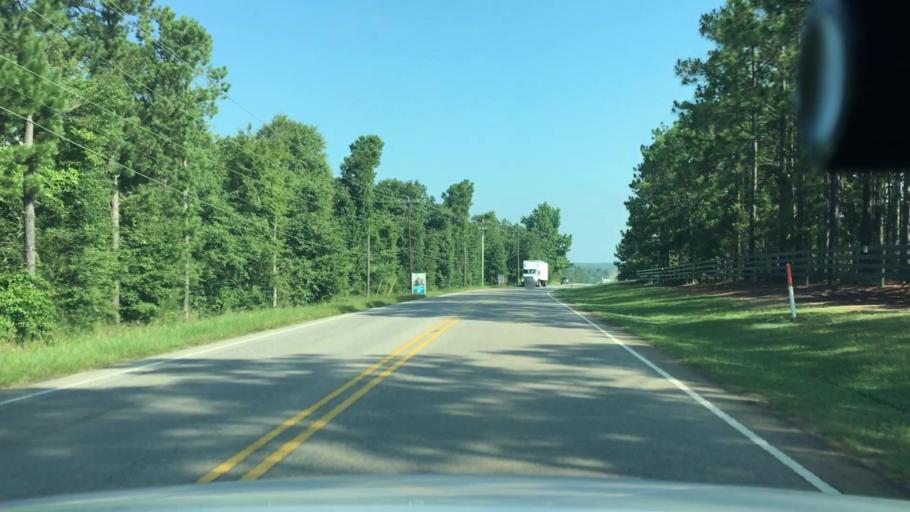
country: US
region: South Carolina
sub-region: Aiken County
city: Graniteville
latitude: 33.5999
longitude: -81.8410
